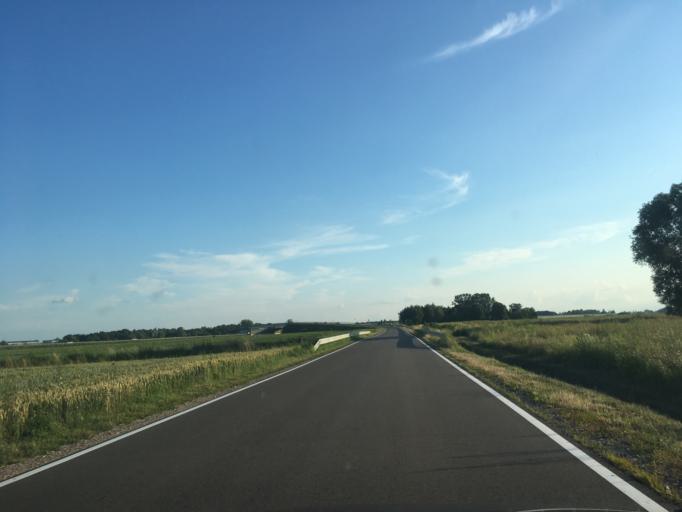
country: PL
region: Masovian Voivodeship
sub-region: Powiat warszawski zachodni
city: Bieniewice
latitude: 52.1466
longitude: 20.6000
